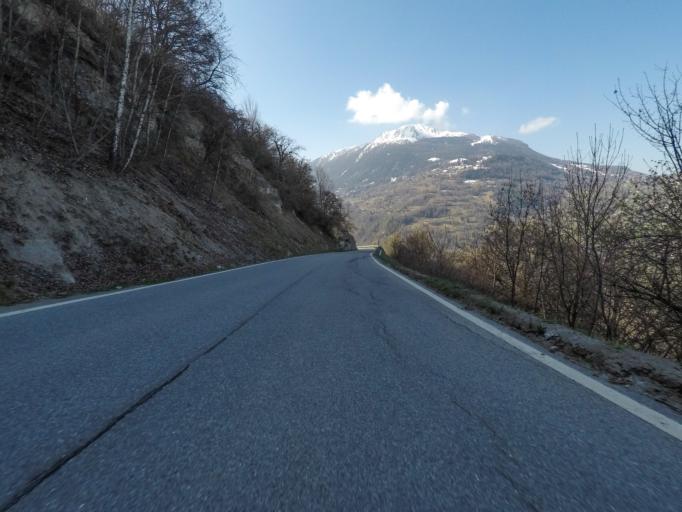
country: CH
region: Valais
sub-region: Conthey District
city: Basse-Nendaz
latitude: 46.1955
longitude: 7.3322
